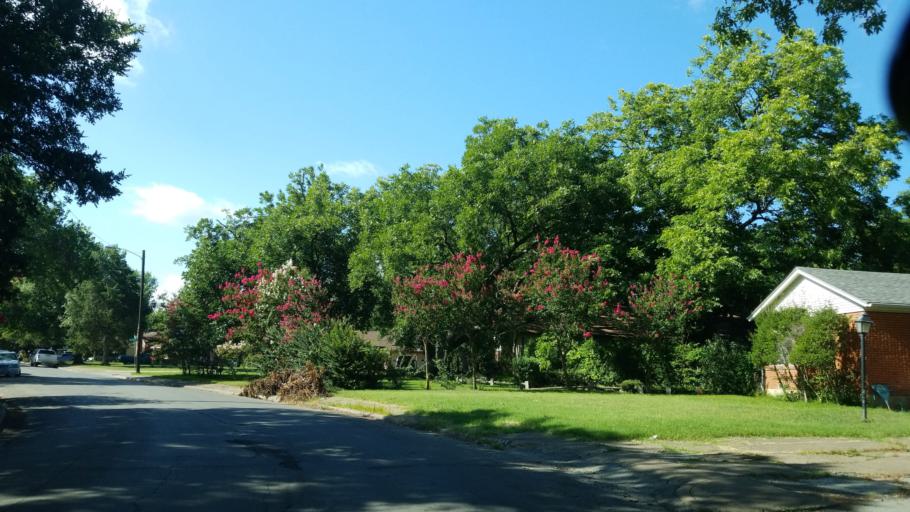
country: US
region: Texas
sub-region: Dallas County
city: Dallas
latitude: 32.7167
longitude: -96.7998
